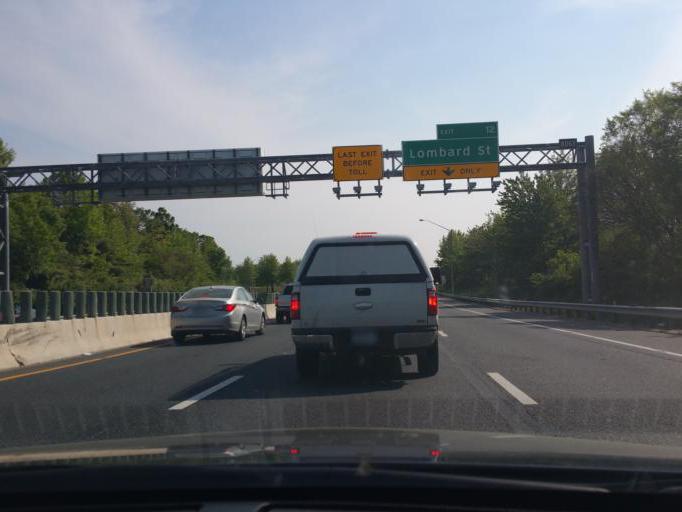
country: US
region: Maryland
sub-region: Baltimore County
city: Rosedale
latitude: 39.2954
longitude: -76.5516
